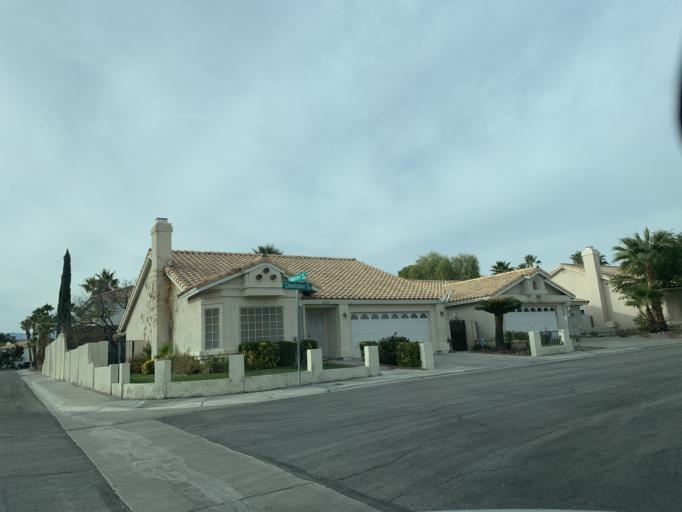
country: US
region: Nevada
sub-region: Clark County
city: Summerlin South
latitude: 36.1413
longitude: -115.2990
